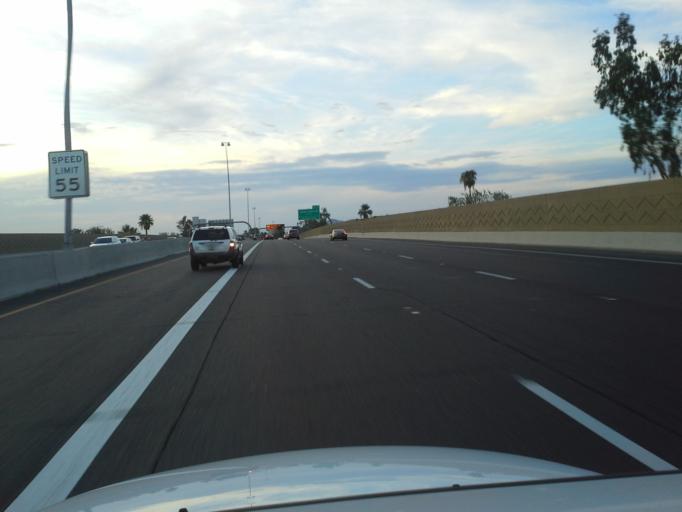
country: US
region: Arizona
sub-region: Maricopa County
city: Phoenix
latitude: 33.4861
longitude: -112.0413
